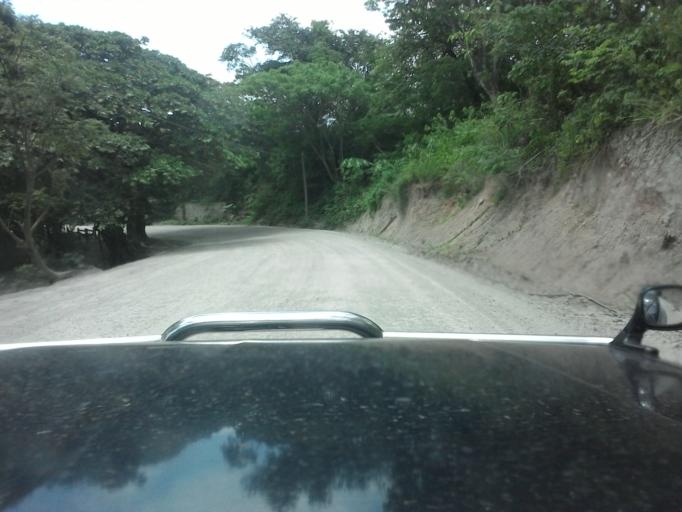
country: CR
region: Guanacaste
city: Juntas
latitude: 10.2435
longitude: -84.8468
